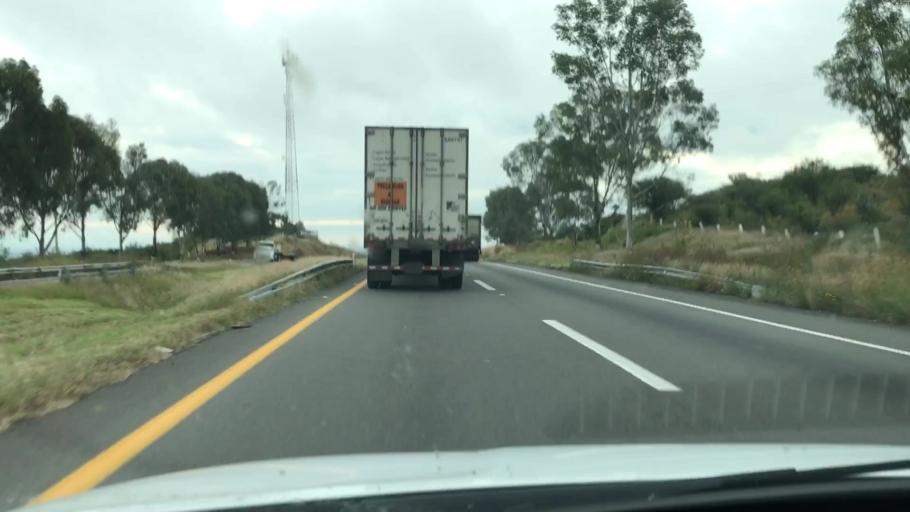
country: MX
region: Jalisco
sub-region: Lagos de Moreno
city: Cristeros [Fraccionamiento]
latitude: 21.2643
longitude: -101.9616
